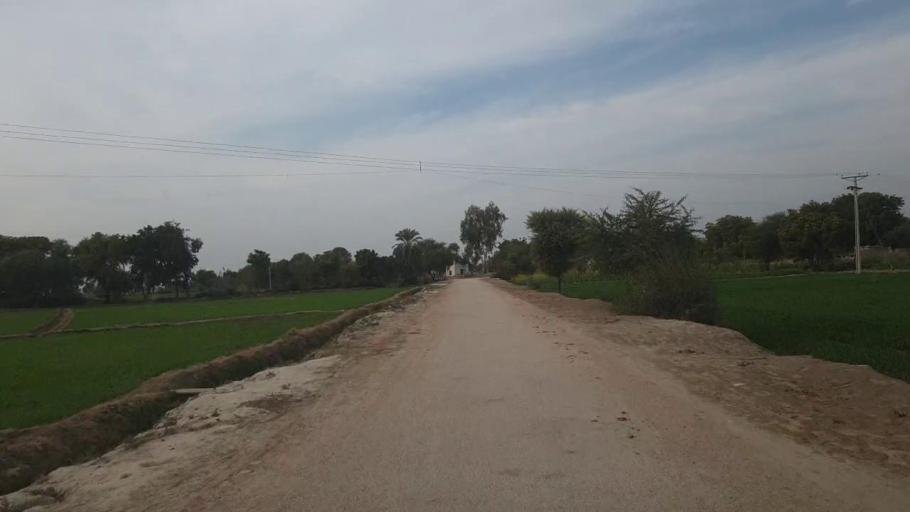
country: PK
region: Sindh
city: Shahpur Chakar
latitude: 26.1148
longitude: 68.5202
